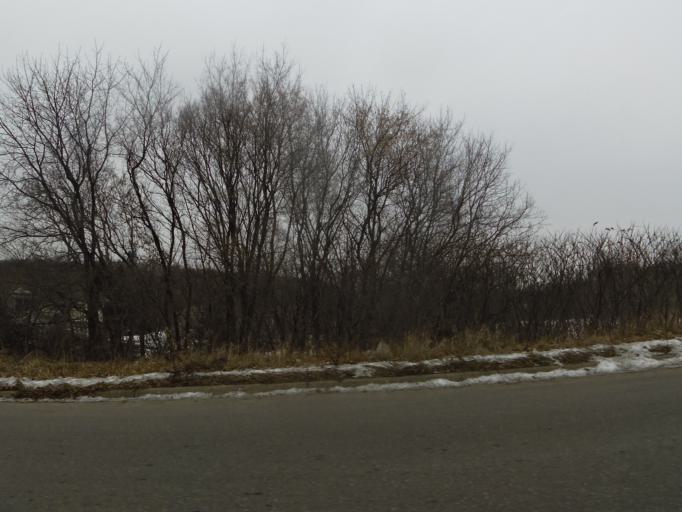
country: US
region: Minnesota
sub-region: Scott County
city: Jordan
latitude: 44.6565
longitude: -93.6317
